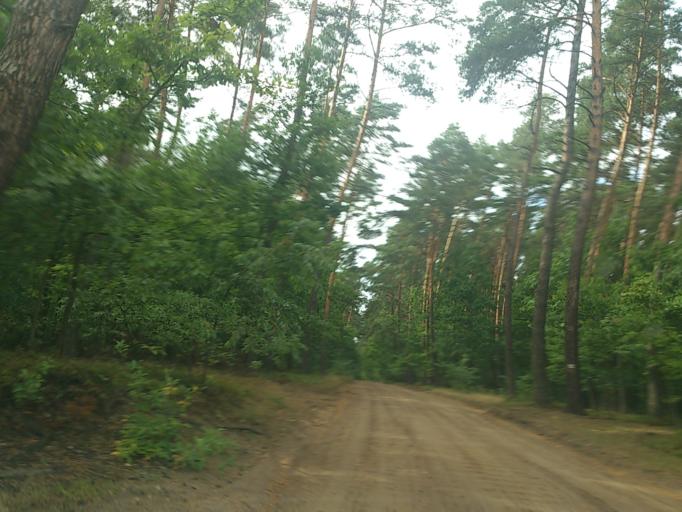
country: PL
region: Greater Poland Voivodeship
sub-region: Powiat poznanski
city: Kobylnica
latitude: 52.5242
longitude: 17.1260
